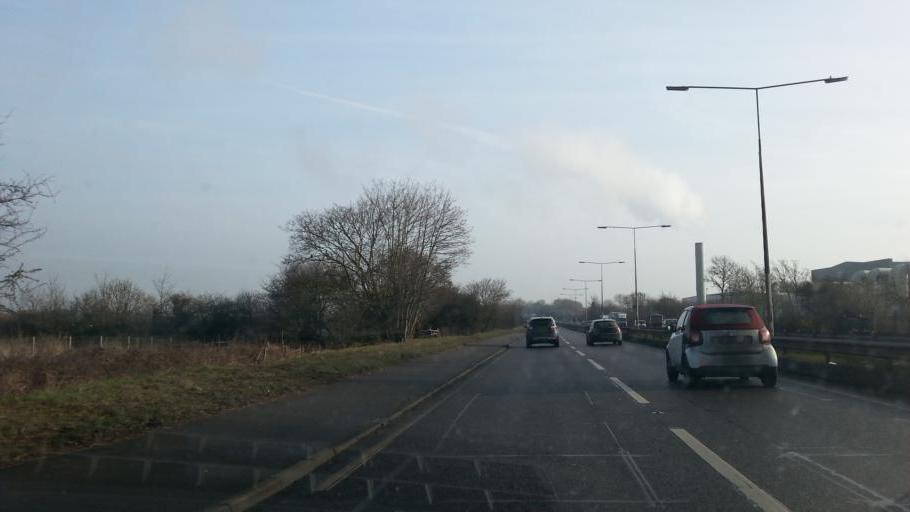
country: GB
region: England
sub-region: Essex
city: Wickford
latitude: 51.5914
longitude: 0.5130
